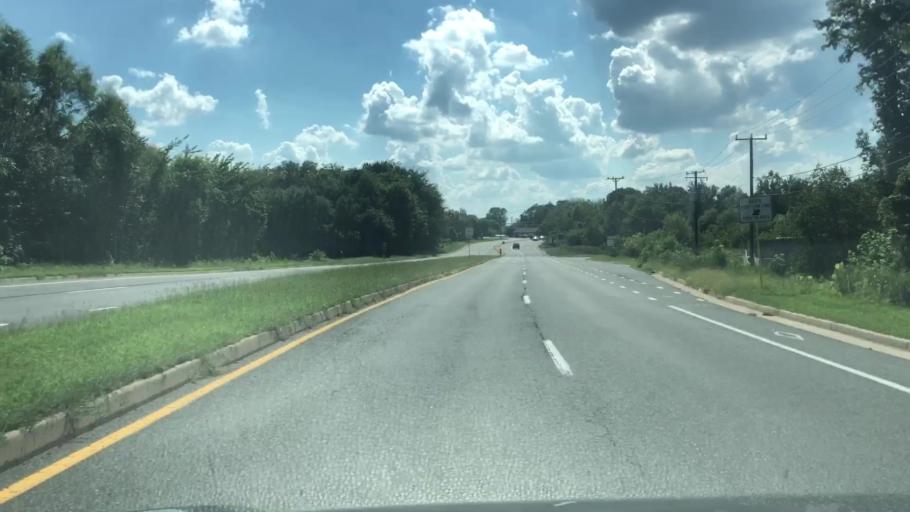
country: US
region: Virginia
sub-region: City of Fredericksburg
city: Fredericksburg
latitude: 38.3028
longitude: -77.4441
